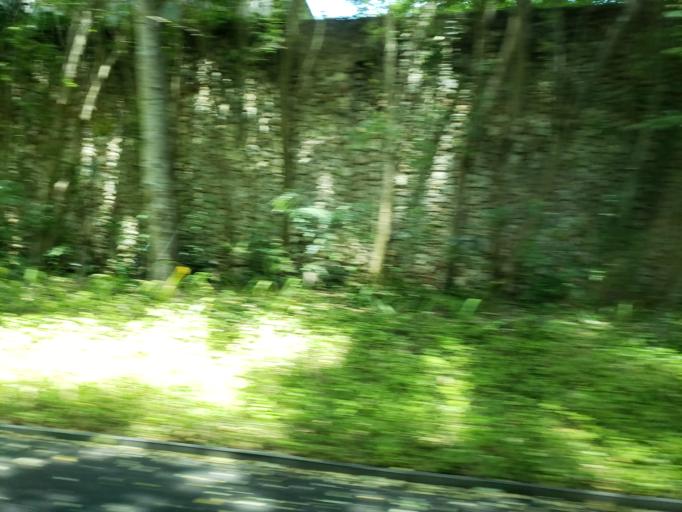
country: ID
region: Bali
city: Kangin
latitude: -8.8439
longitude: 115.1381
